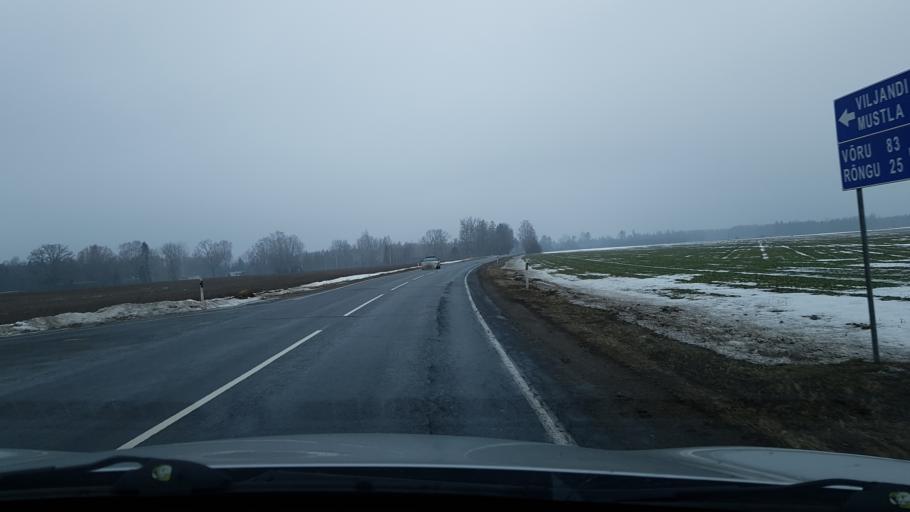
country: EE
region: Valgamaa
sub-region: Torva linn
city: Torva
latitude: 58.1543
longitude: 25.9652
